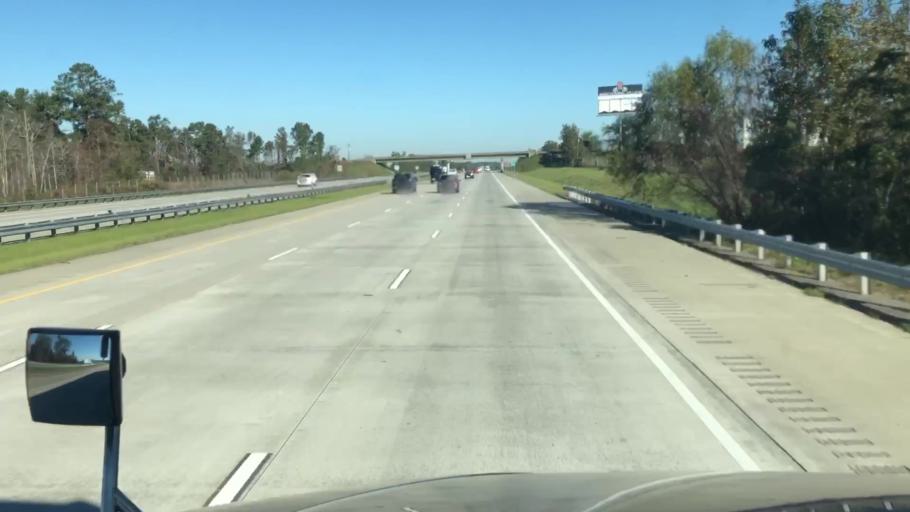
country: US
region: Georgia
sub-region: Dooly County
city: Unadilla
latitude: 32.2875
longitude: -83.7579
